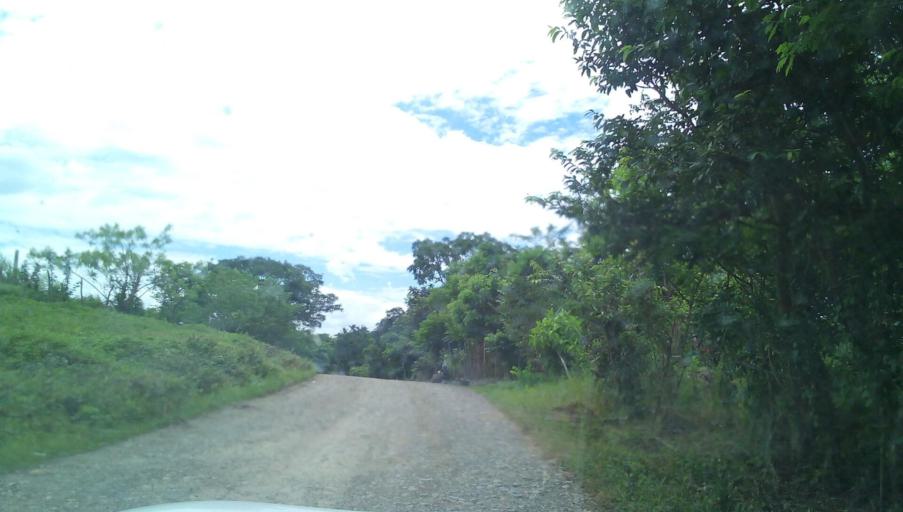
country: MX
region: Veracruz
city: Tepetzintla
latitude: 21.1509
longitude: -97.8557
